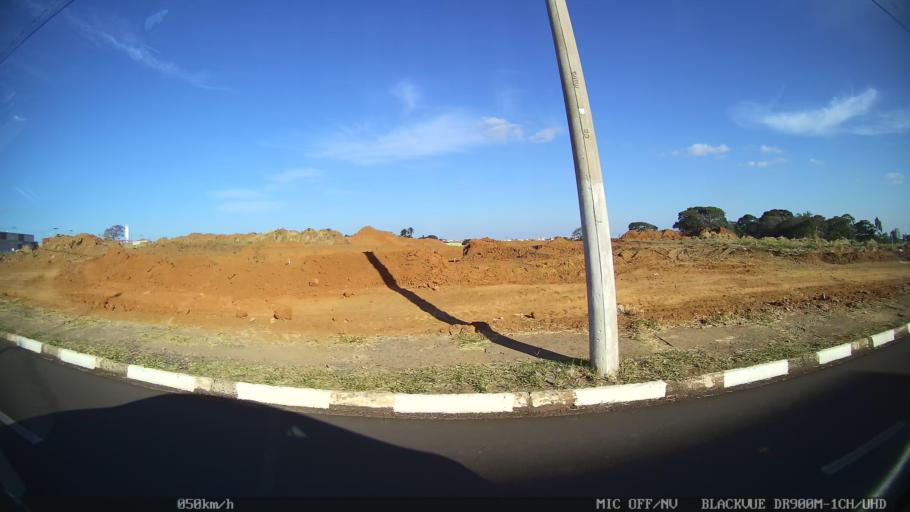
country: BR
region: Sao Paulo
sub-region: Franca
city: Franca
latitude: -20.5146
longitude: -47.3755
